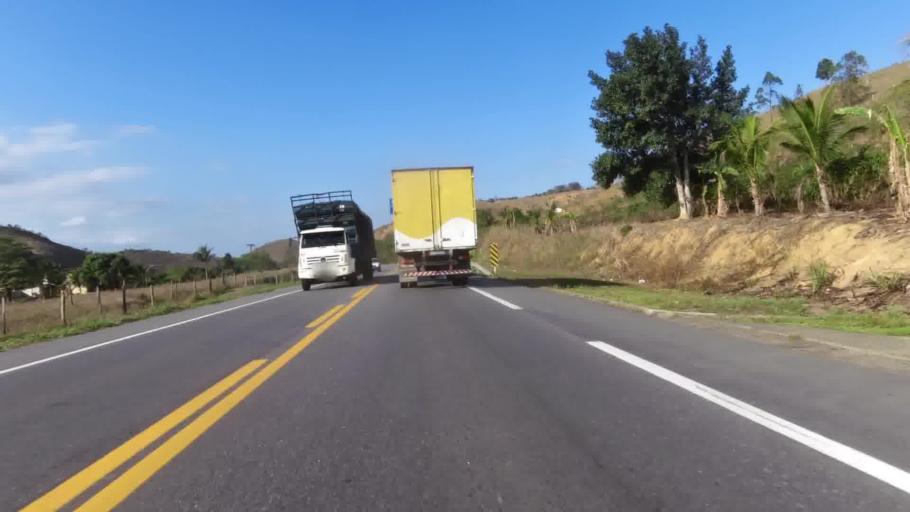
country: BR
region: Espirito Santo
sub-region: Mimoso Do Sul
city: Mimoso do Sul
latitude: -21.1743
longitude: -41.2952
